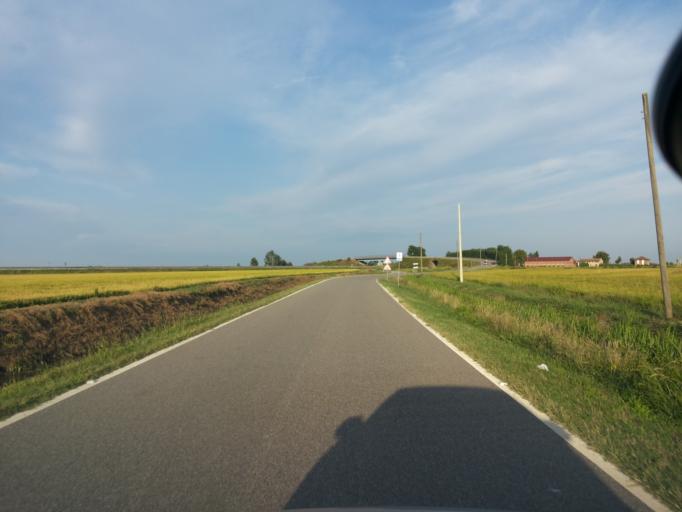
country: IT
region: Piedmont
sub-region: Provincia di Vercelli
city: Salasco
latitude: 45.3247
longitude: 8.2377
